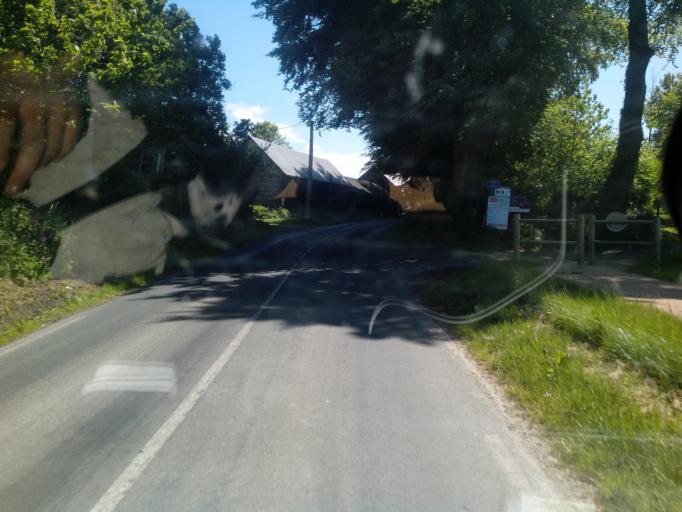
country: FR
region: Haute-Normandie
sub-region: Departement de la Seine-Maritime
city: Turretot
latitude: 49.6337
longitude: 0.2703
